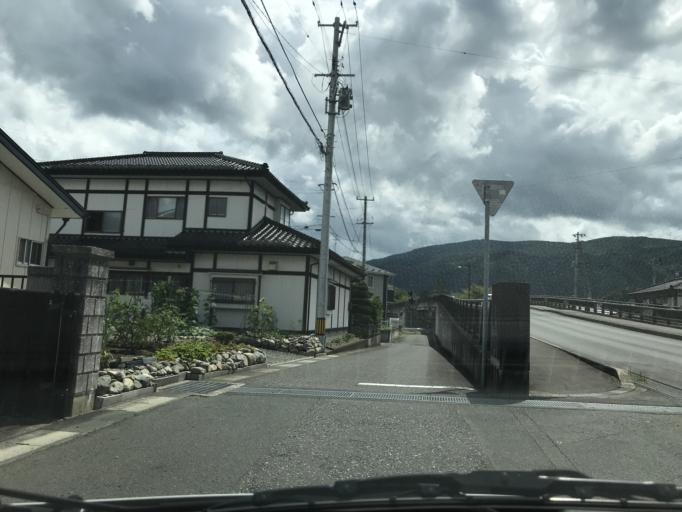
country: JP
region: Iwate
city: Tono
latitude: 39.3324
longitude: 141.5374
